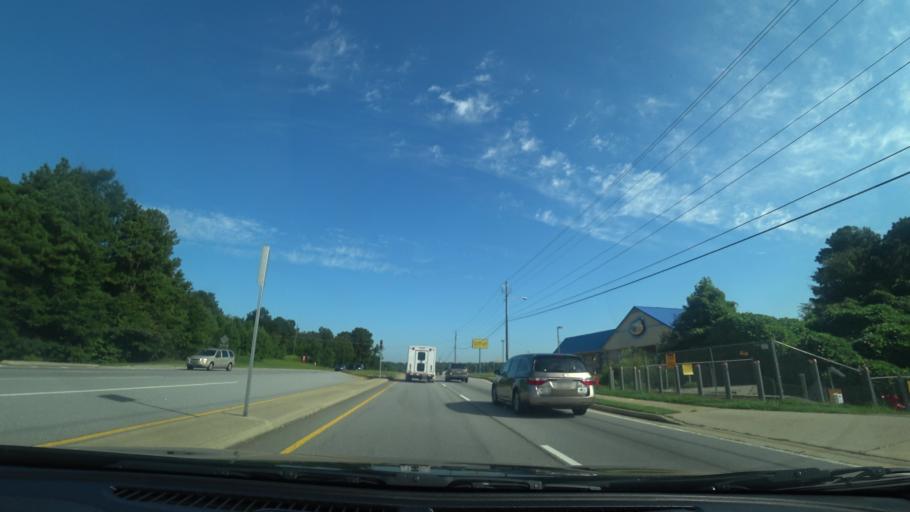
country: US
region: Georgia
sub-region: Gwinnett County
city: Grayson
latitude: 33.9208
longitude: -83.9728
